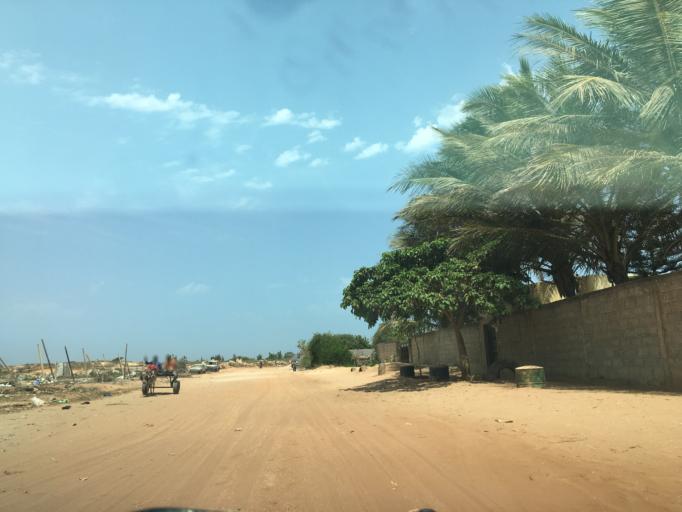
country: SN
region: Thies
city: Thies
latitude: 14.8069
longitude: -17.1882
